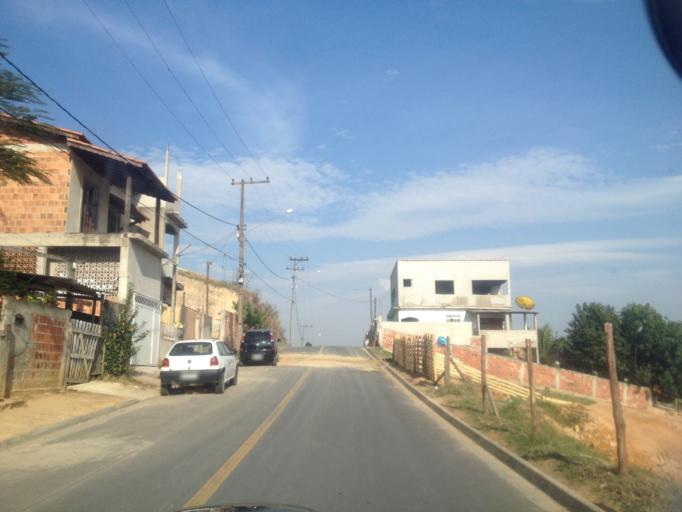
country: BR
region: Rio de Janeiro
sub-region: Porto Real
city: Porto Real
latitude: -22.4418
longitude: -44.3226
